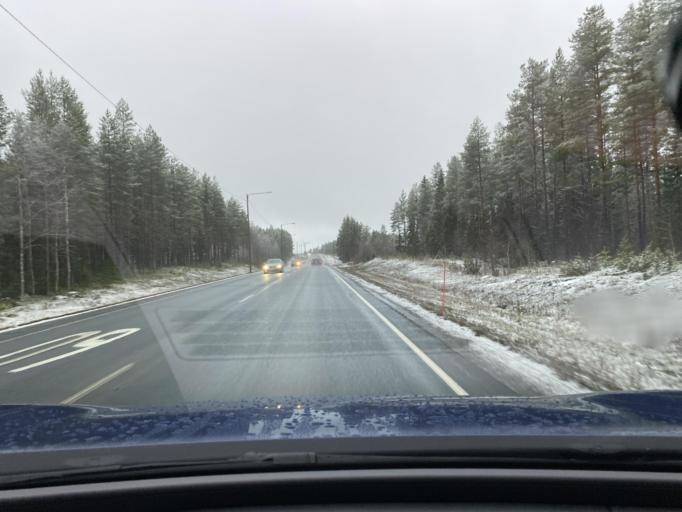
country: FI
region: Northern Ostrobothnia
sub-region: Oulu
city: Kiiminki
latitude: 65.1253
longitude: 25.7636
